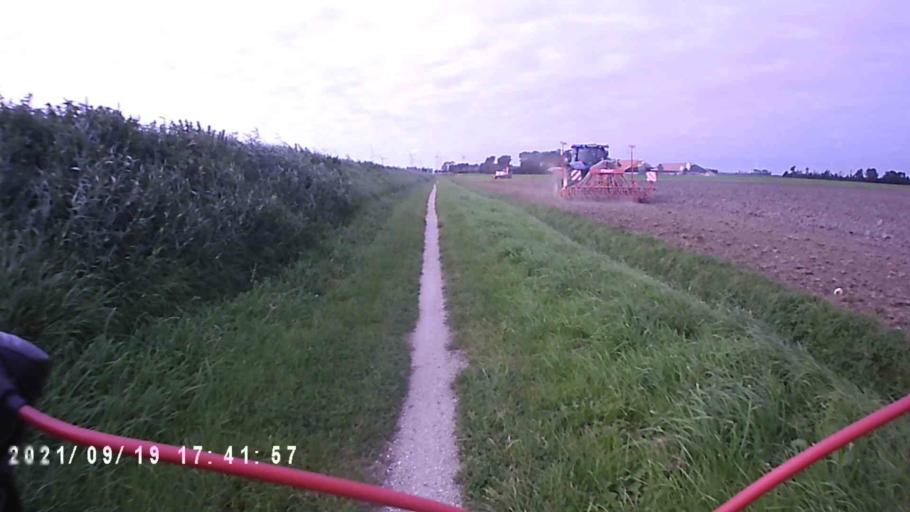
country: NL
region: Groningen
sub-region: Gemeente Delfzijl
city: Delfzijl
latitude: 53.2565
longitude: 6.9708
